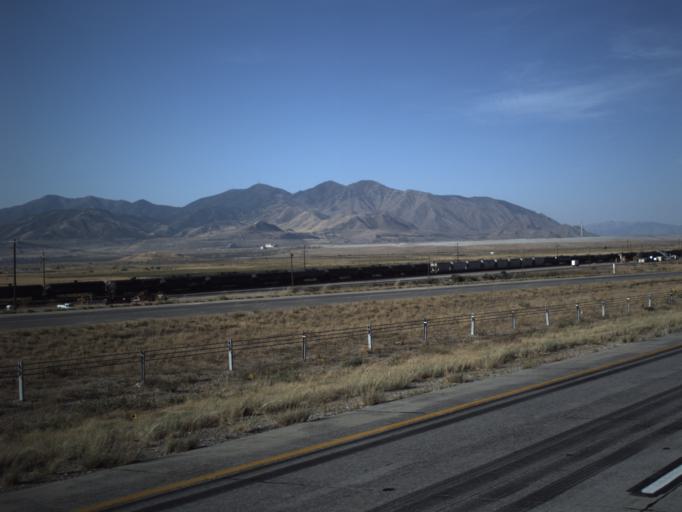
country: US
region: Utah
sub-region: Salt Lake County
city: Magna
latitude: 40.7712
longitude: -112.0423
